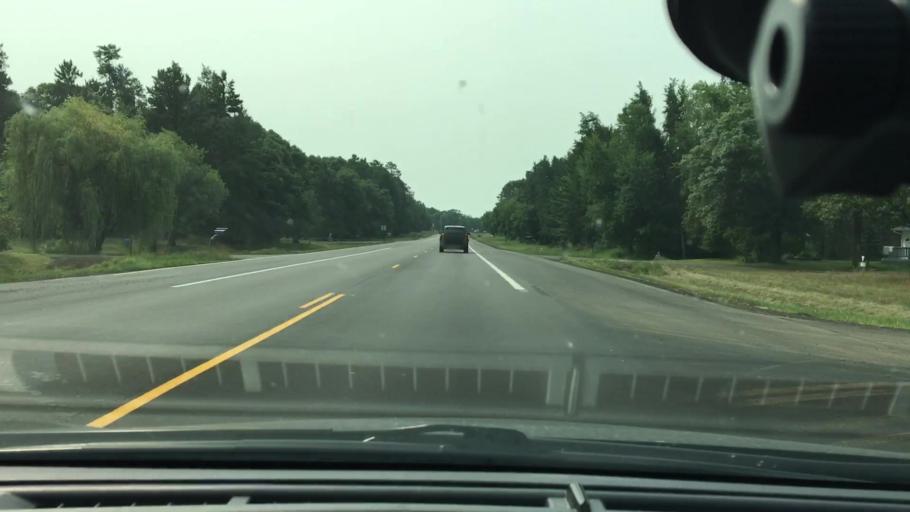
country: US
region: Minnesota
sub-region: Crow Wing County
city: Brainerd
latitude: 46.4422
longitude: -94.1717
